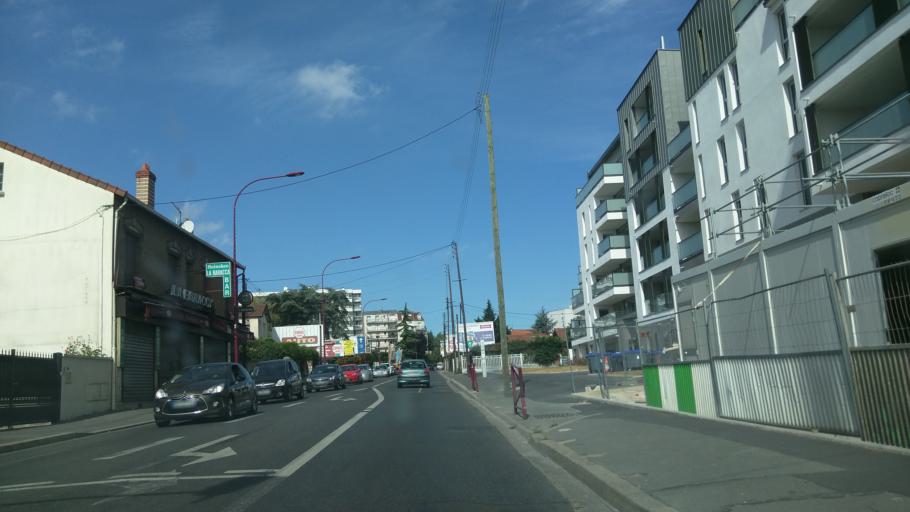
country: FR
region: Ile-de-France
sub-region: Departement du Val-d'Oise
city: Bezons
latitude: 48.9343
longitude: 2.2091
